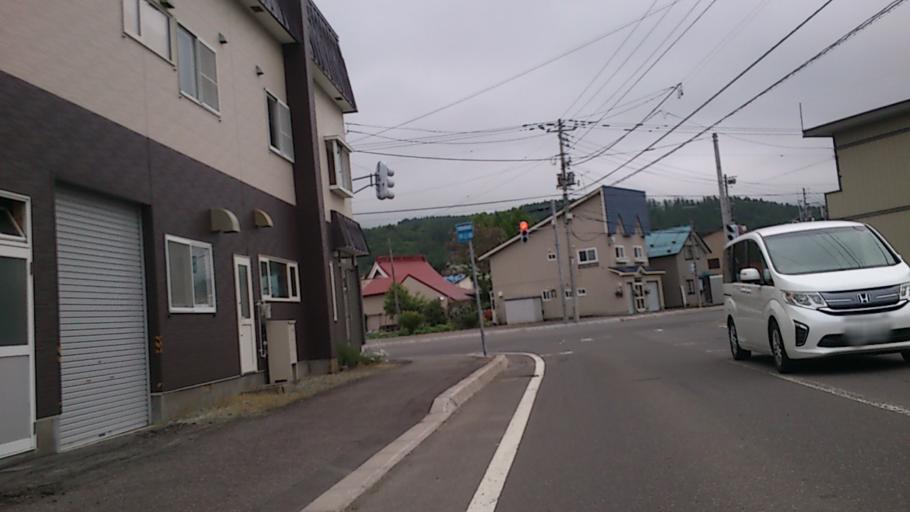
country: JP
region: Hokkaido
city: Niseko Town
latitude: 42.8083
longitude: 140.5296
